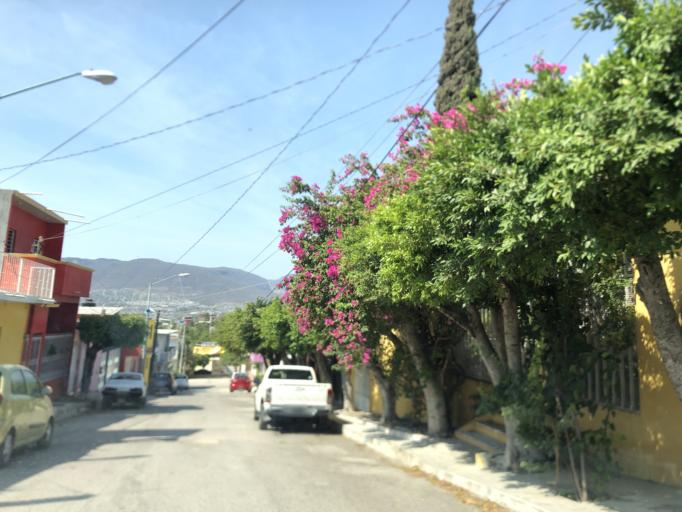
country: MX
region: Chiapas
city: Tuxtla Gutierrez
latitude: 16.7391
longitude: -93.1007
